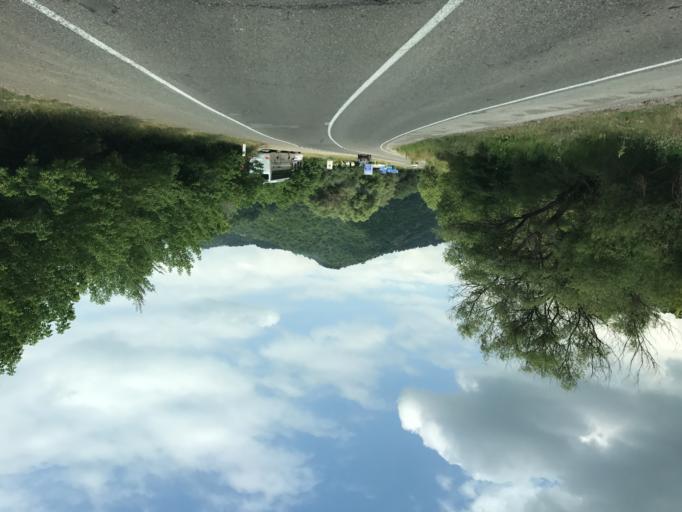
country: AM
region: Tavush
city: Dilijan
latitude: 40.7620
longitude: 44.9135
